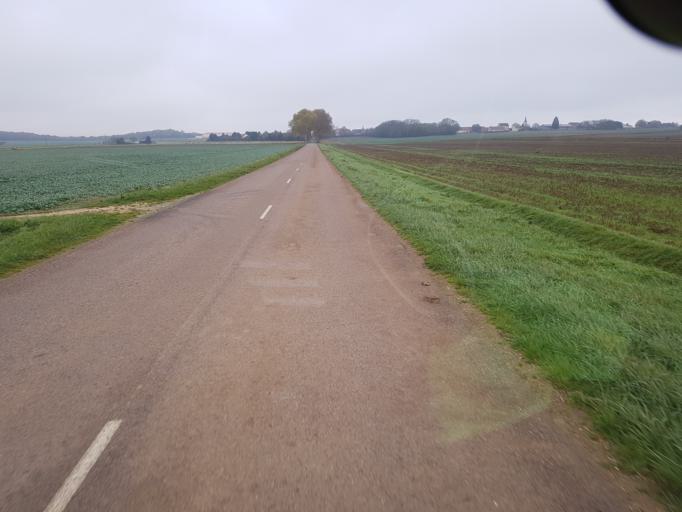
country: FR
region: Bourgogne
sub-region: Departement de la Cote-d'Or
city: Saint-Julien
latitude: 47.4330
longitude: 5.2178
